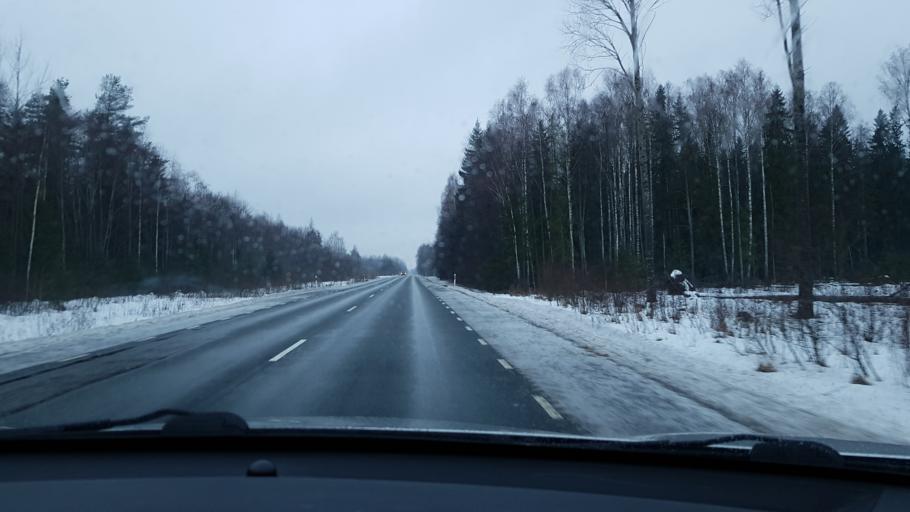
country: EE
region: Jaervamaa
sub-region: Tueri vald
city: Sarevere
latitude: 58.8015
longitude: 25.2313
